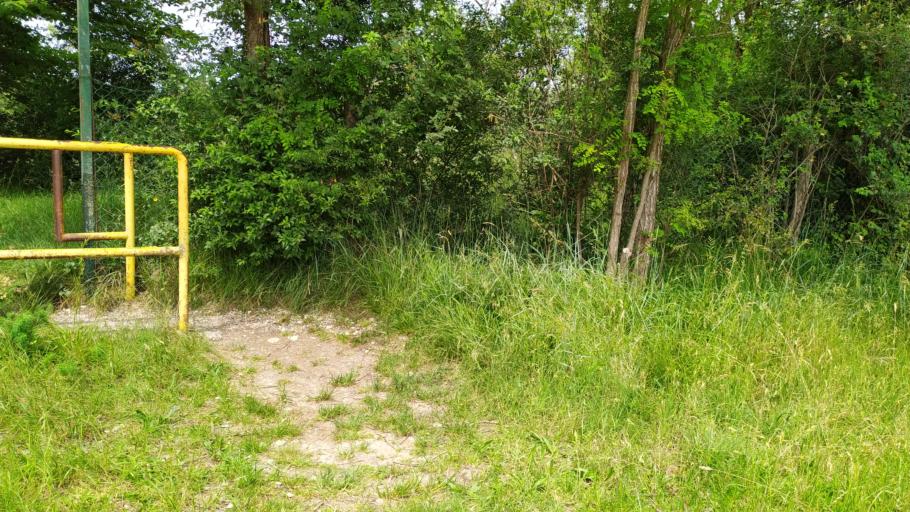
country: IT
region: Veneto
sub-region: Provincia di Treviso
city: Moriago della Battaglia
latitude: 45.8453
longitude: 12.1153
